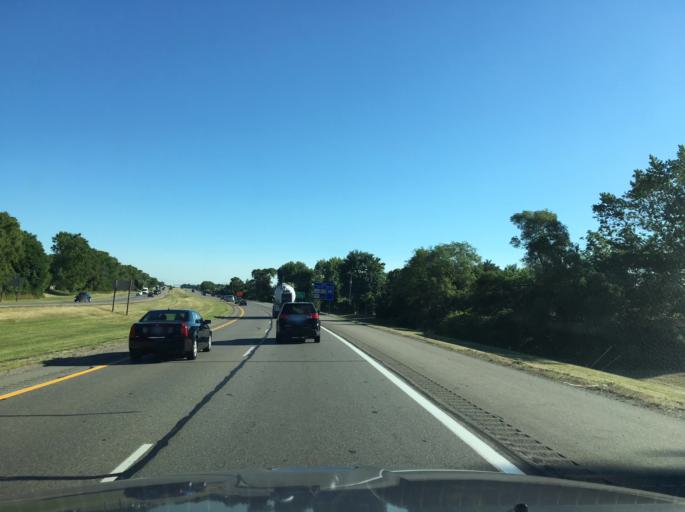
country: US
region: Michigan
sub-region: Macomb County
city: Utica
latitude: 42.6123
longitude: -83.0119
